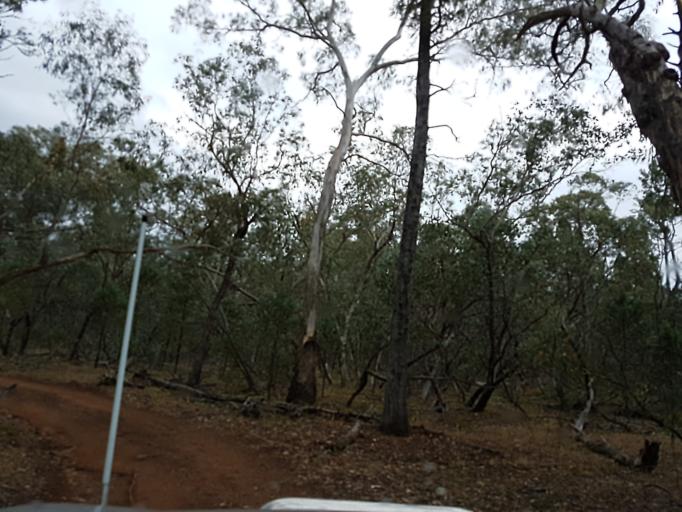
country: AU
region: New South Wales
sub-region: Snowy River
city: Jindabyne
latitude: -36.9441
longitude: 148.3942
